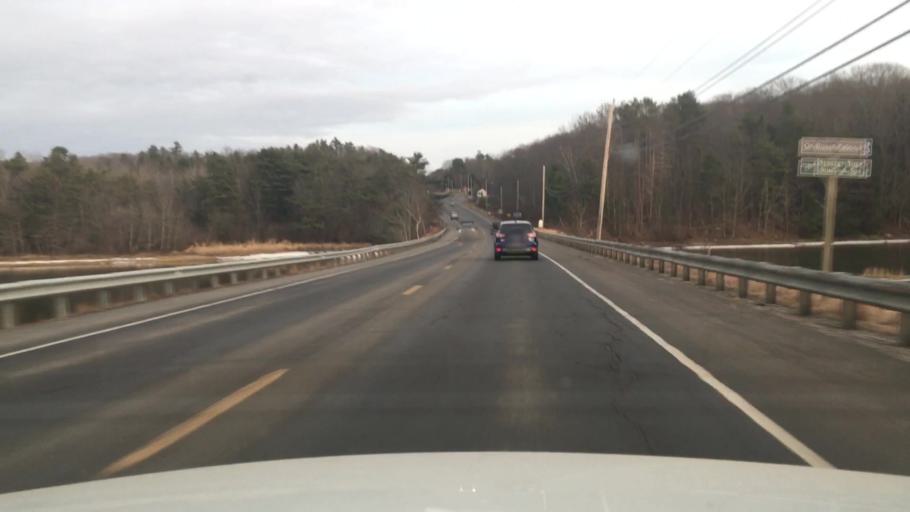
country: US
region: Maine
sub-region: Lincoln County
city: Wiscasset
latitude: 44.0003
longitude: -69.6416
